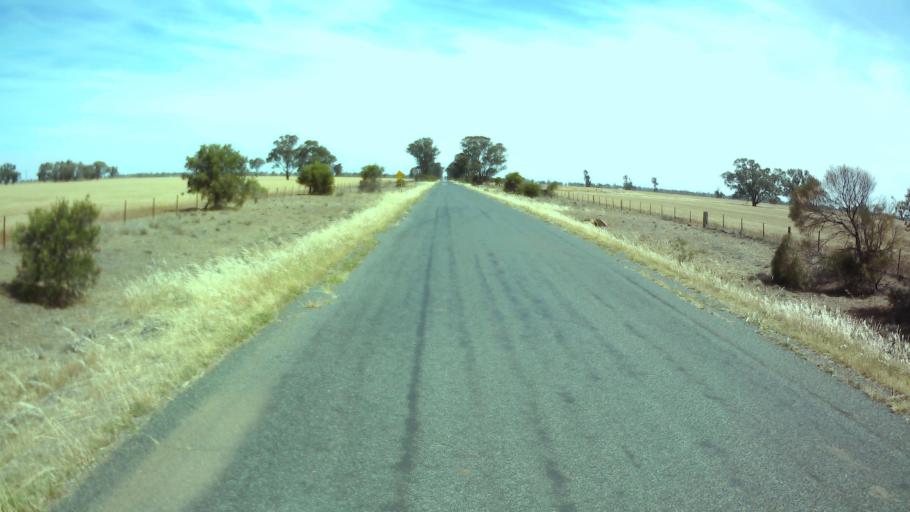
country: AU
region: New South Wales
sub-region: Weddin
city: Grenfell
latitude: -33.9662
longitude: 147.7808
